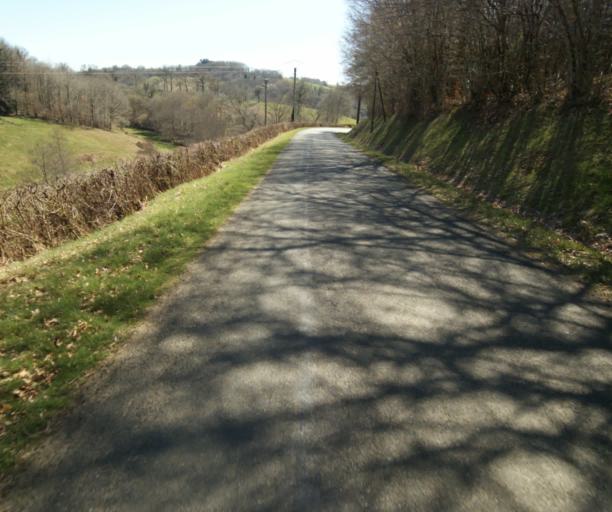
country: FR
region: Limousin
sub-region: Departement de la Correze
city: Chamboulive
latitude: 45.4556
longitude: 1.6736
